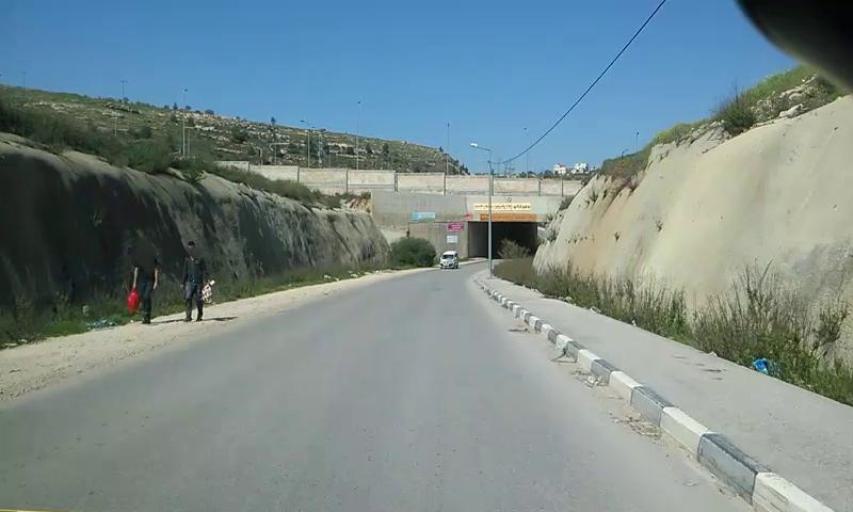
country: PS
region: West Bank
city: Al Khadir
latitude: 31.7037
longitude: 35.1585
